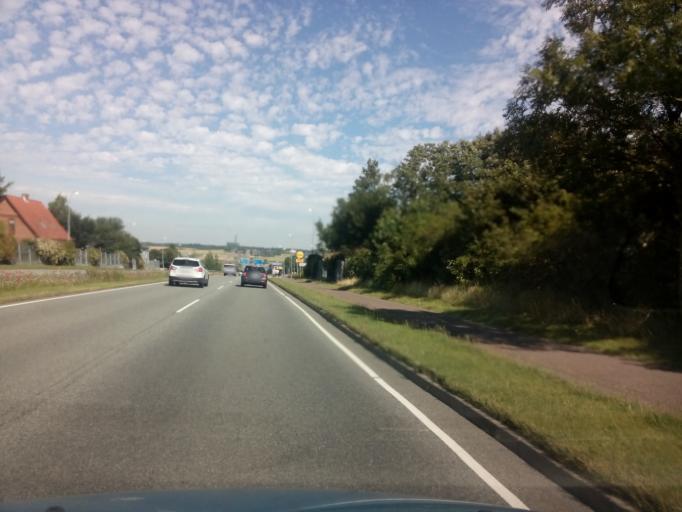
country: DK
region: Central Jutland
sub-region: Arhus Kommune
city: Arhus
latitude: 56.1984
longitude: 10.1831
